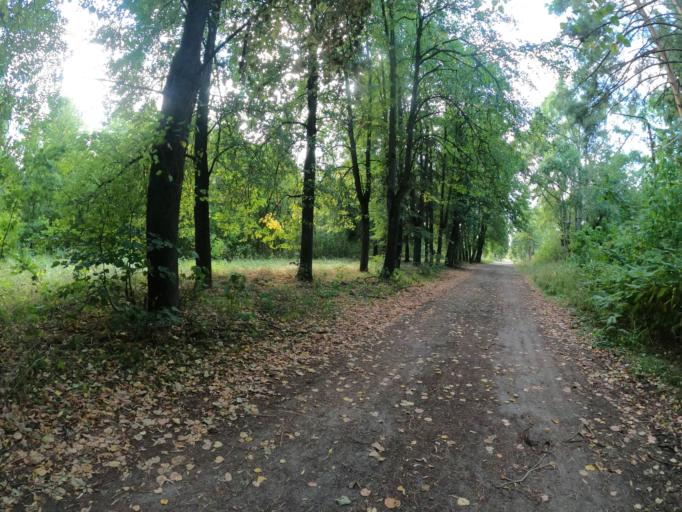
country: RU
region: Moskovskaya
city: Konobeyevo
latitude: 55.3910
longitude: 38.7103
